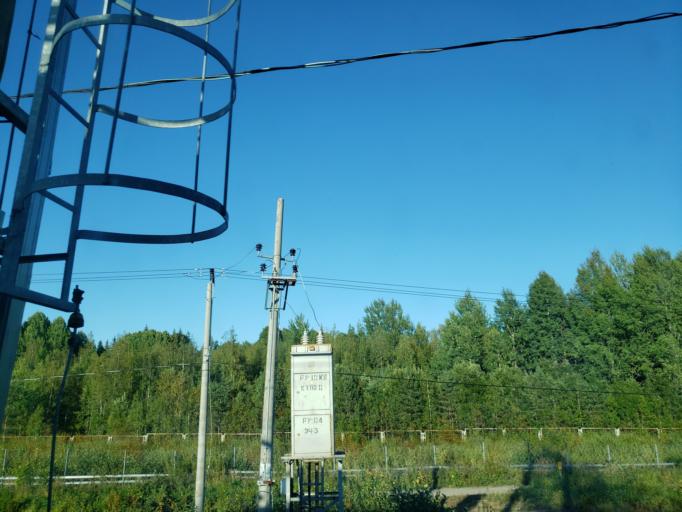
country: FI
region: South Karelia
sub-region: Lappeenranta
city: Nuijamaa
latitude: 60.8473
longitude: 28.3694
